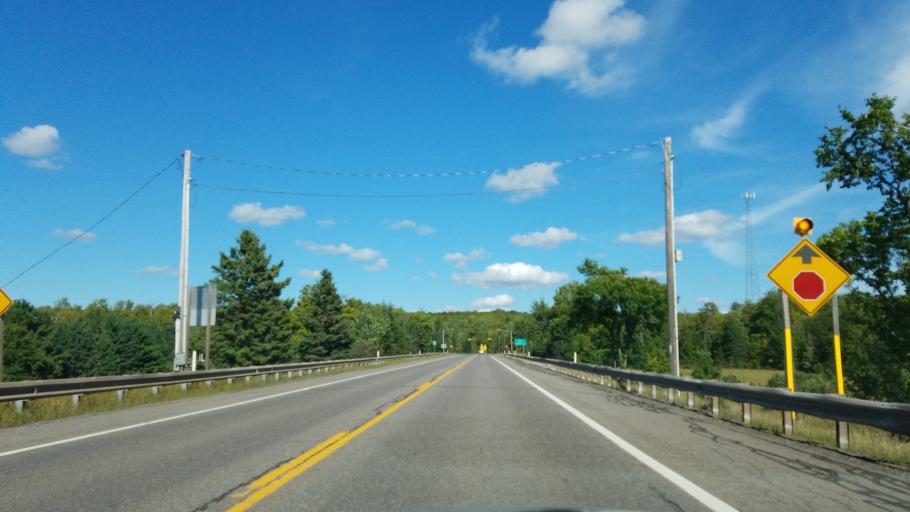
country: US
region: Michigan
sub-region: Baraga County
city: L'Anse
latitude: 46.5840
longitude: -88.4757
